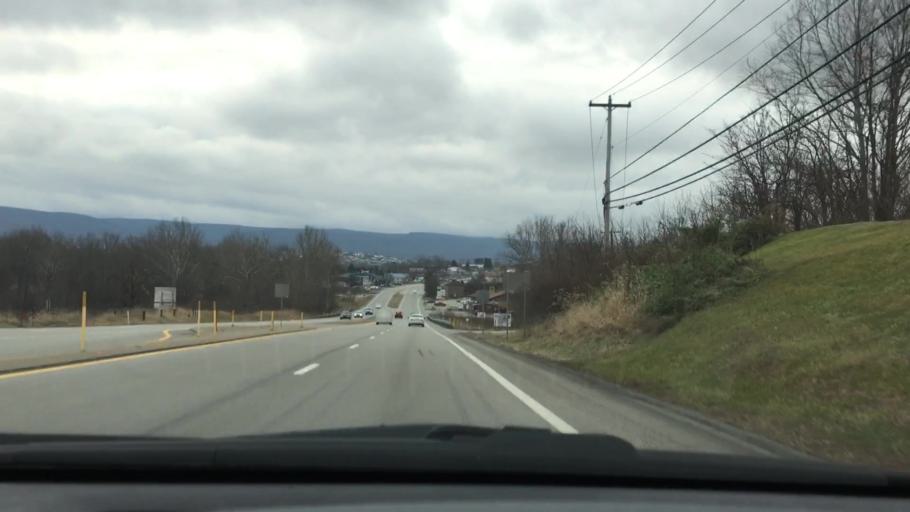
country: US
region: Pennsylvania
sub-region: Fayette County
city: Oliver
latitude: 39.9311
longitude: -79.7288
